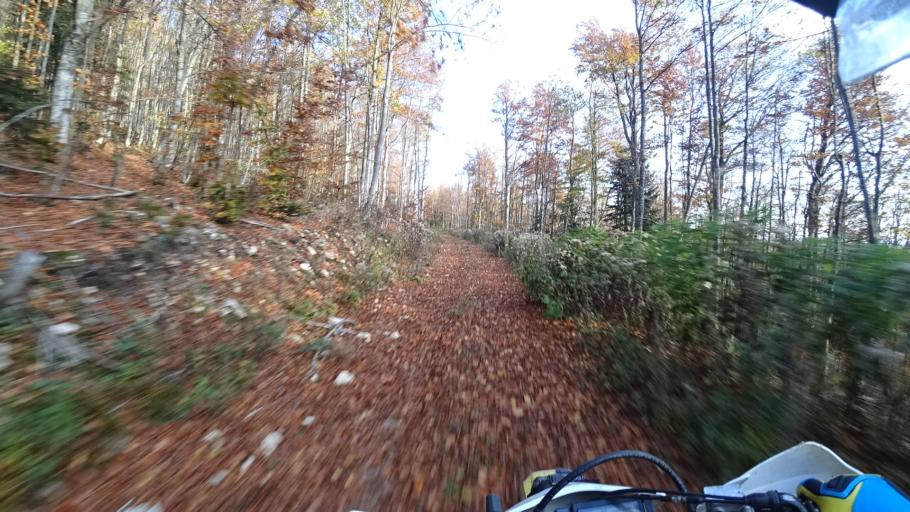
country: HR
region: Karlovacka
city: Plaski
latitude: 44.9544
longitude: 15.3991
